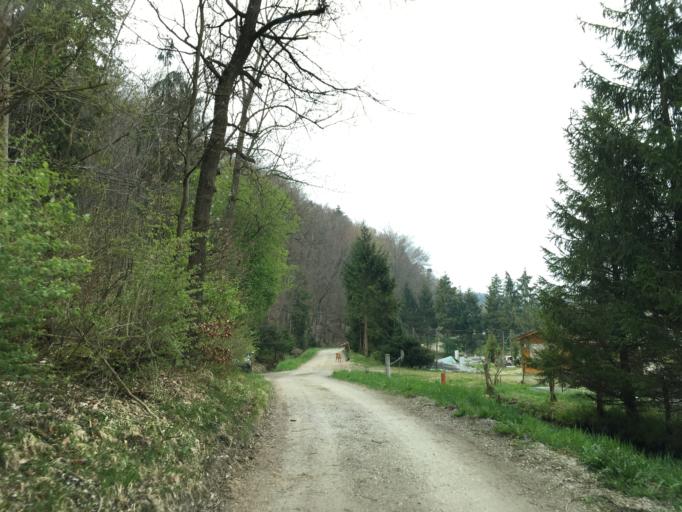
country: DE
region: Bavaria
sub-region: Upper Bavaria
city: Jettenbach
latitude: 48.1609
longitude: 12.3703
